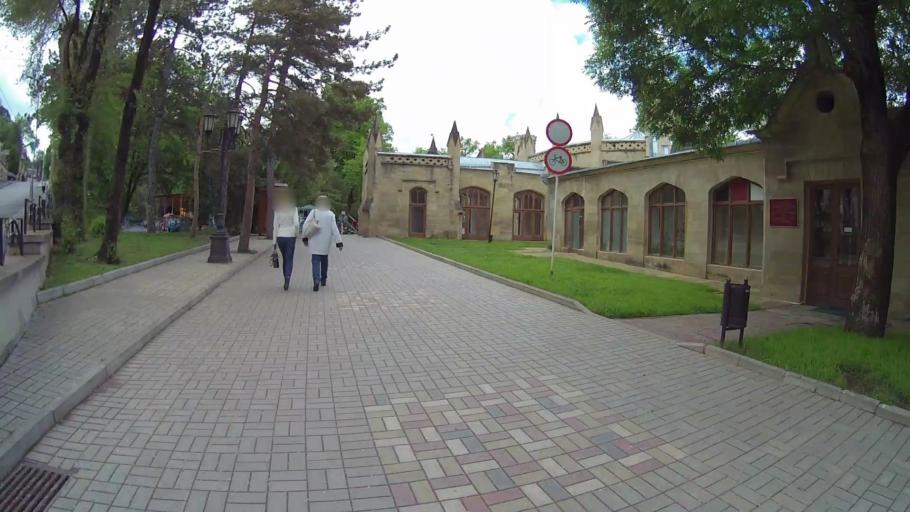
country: RU
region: Stavropol'skiy
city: Kislovodsk
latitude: 43.8999
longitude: 42.7173
